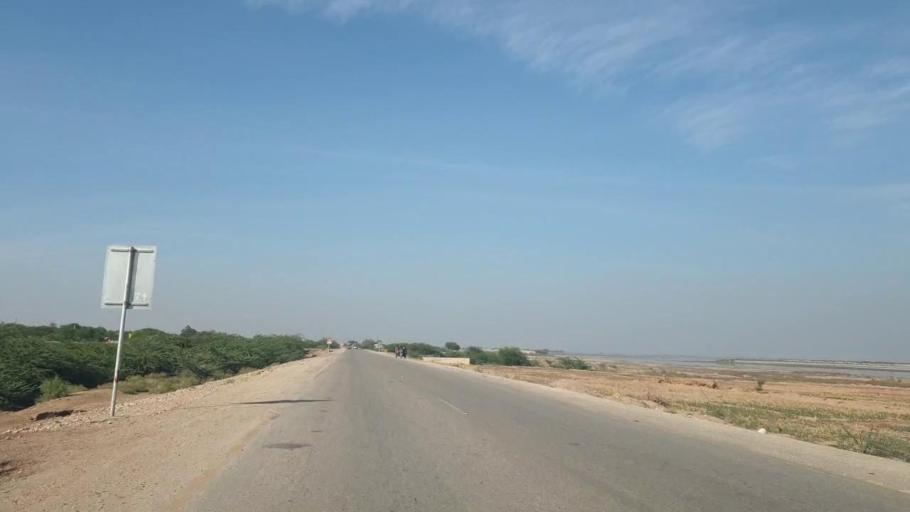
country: PK
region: Sindh
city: Sehwan
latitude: 26.3781
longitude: 67.8726
